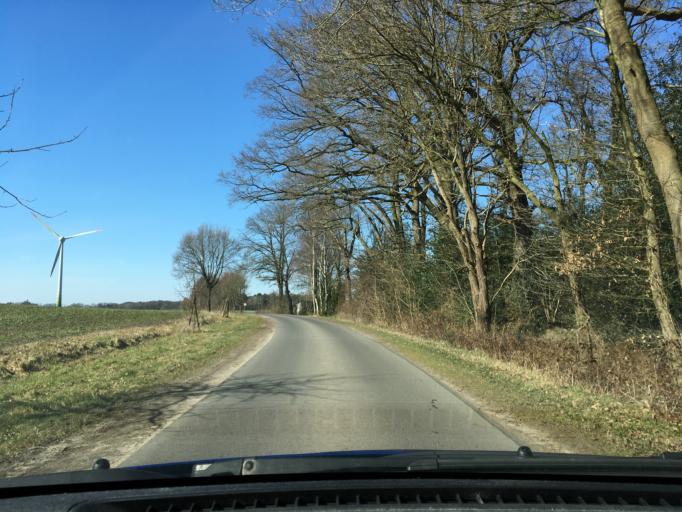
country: DE
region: Lower Saxony
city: Schneverdingen
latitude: 53.0824
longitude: 9.7875
